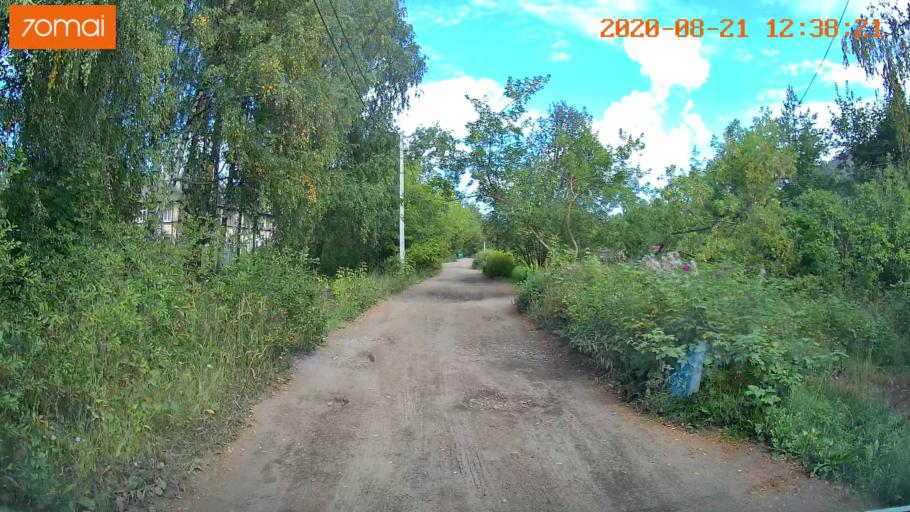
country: RU
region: Ivanovo
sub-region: Gorod Ivanovo
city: Ivanovo
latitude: 57.0062
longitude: 40.9437
